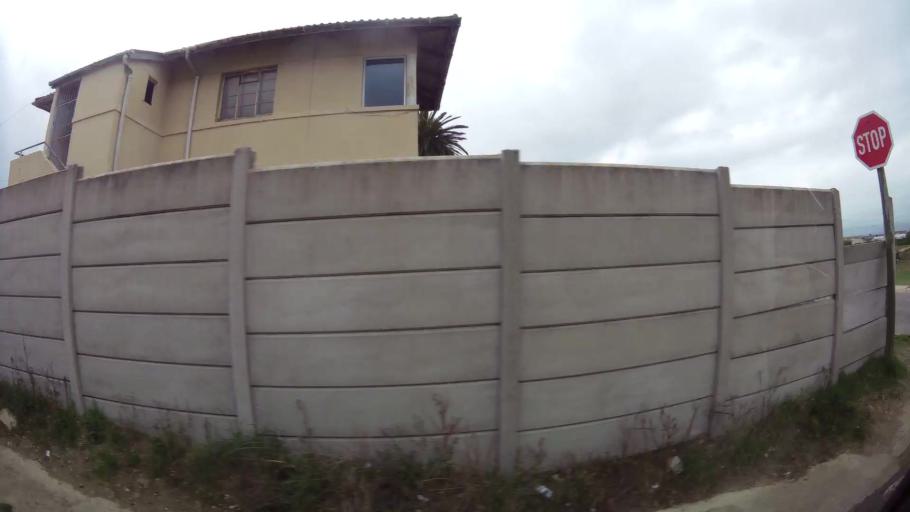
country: ZA
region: Eastern Cape
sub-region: Nelson Mandela Bay Metropolitan Municipality
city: Port Elizabeth
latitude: -33.9097
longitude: 25.5706
